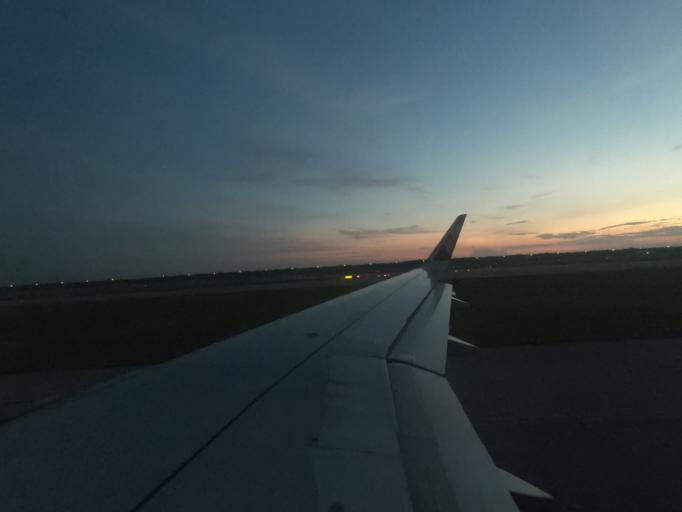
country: MY
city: Sungai Pelek New Village
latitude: 2.7311
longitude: 101.6857
